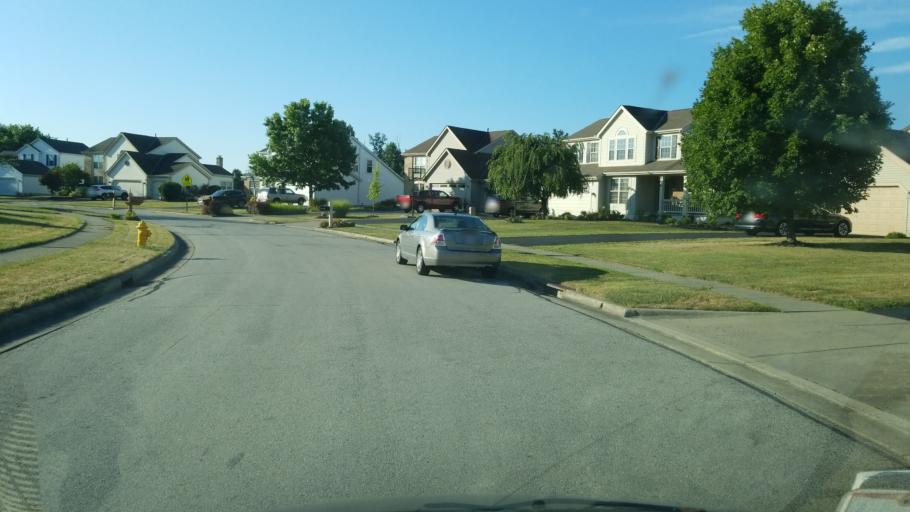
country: US
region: Ohio
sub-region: Delaware County
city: Lewis Center
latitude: 40.1671
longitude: -83.0064
